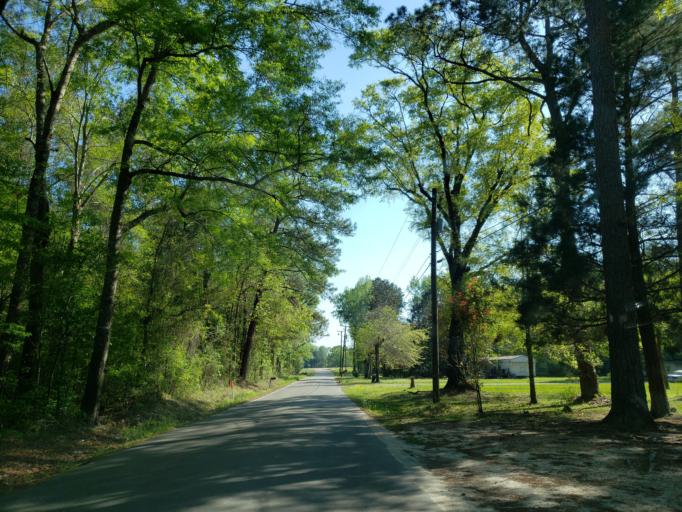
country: US
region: Mississippi
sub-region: Perry County
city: New Augusta
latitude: 31.1630
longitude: -88.9213
